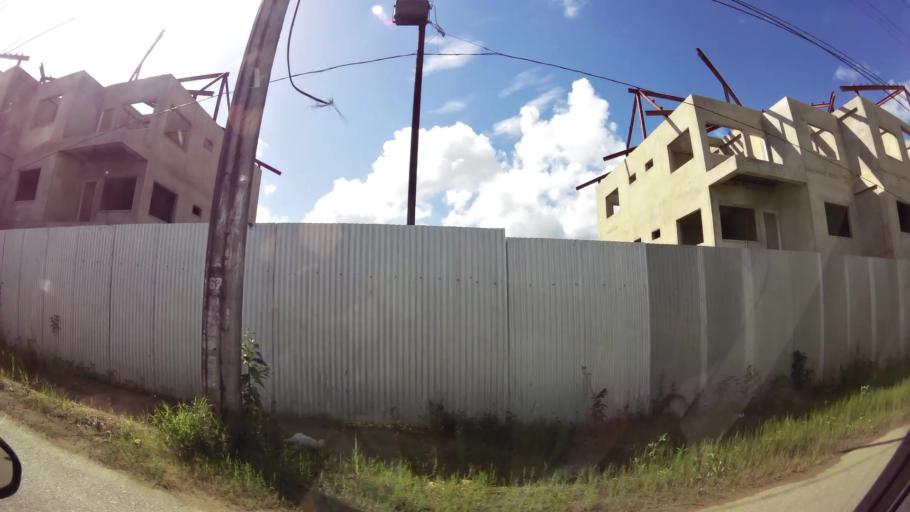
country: TT
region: Chaguanas
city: Chaguanas
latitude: 10.5370
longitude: -61.3905
